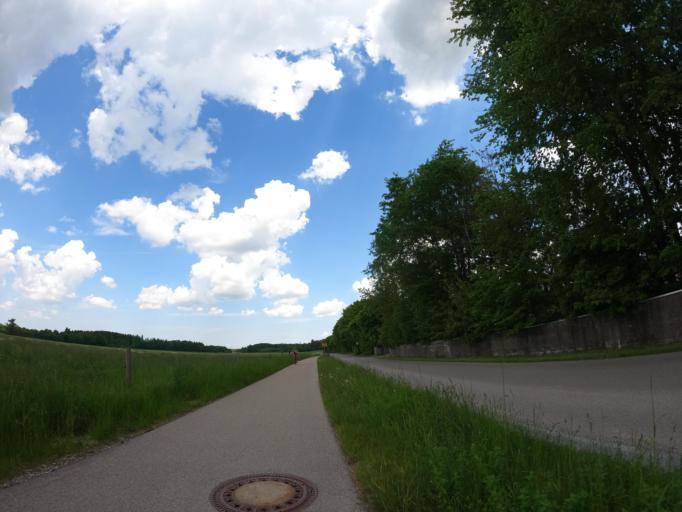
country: DE
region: Bavaria
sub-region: Upper Bavaria
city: Sauerlach
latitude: 47.9819
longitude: 11.6542
